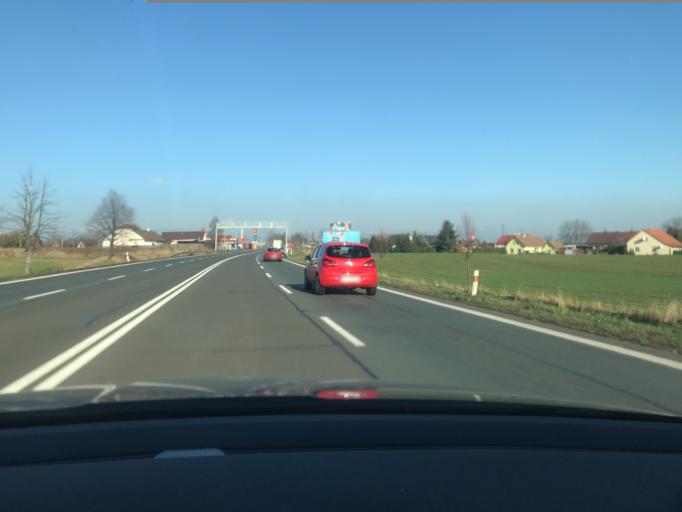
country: CZ
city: Predmerice nad Labem
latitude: 50.2255
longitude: 15.7896
